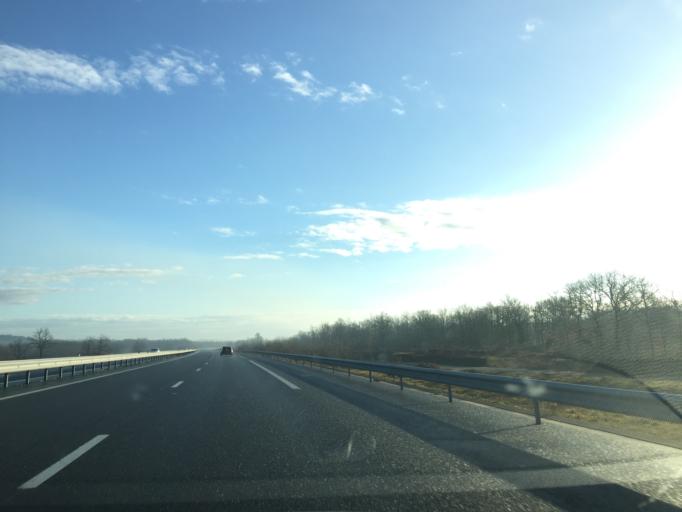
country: FR
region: Aquitaine
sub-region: Departement de la Dordogne
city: Thenon
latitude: 45.1541
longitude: 1.0775
